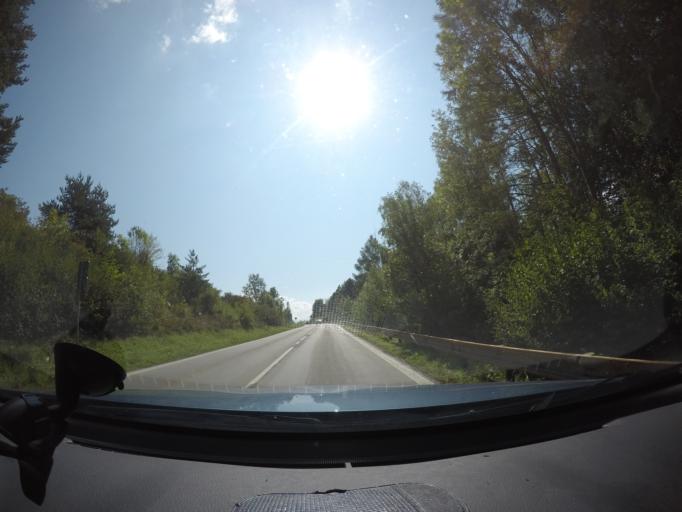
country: SK
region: Zilinsky
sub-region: Okres Liptovsky Mikulas
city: Liptovsky Mikulas
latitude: 49.1333
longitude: 19.5164
